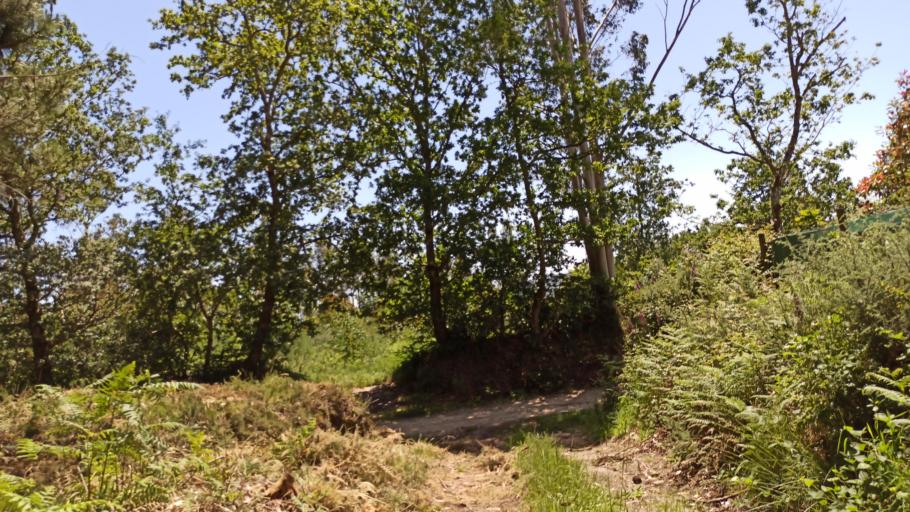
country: ES
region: Galicia
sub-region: Provincia da Coruna
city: Negreira
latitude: 42.9173
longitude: -8.7205
